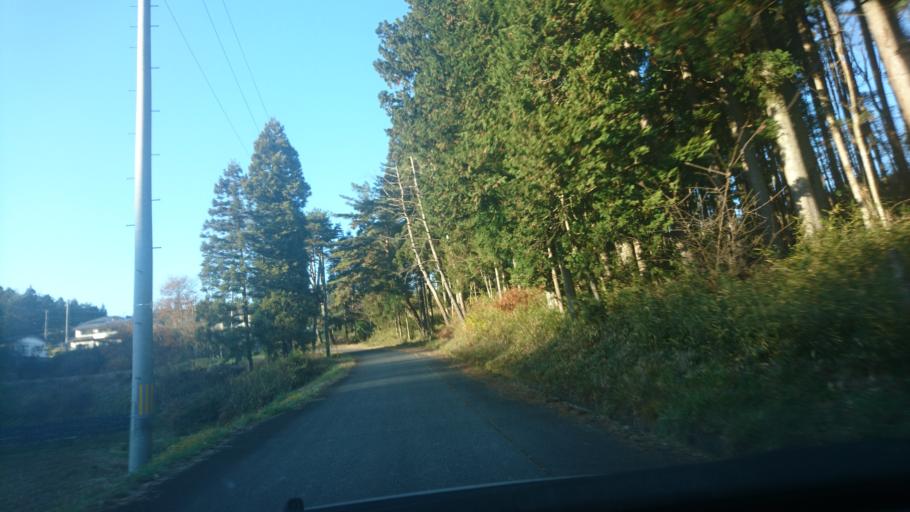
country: JP
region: Iwate
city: Ichinoseki
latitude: 38.9064
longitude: 141.1648
